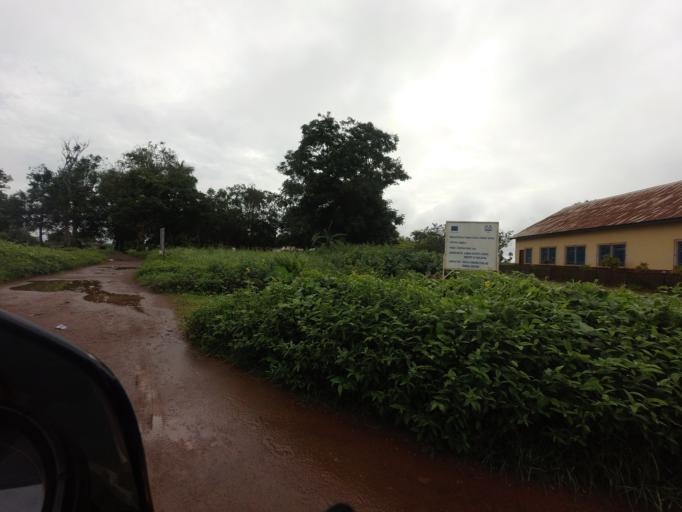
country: SL
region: Northern Province
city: Kambia
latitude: 9.1133
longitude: -12.9244
